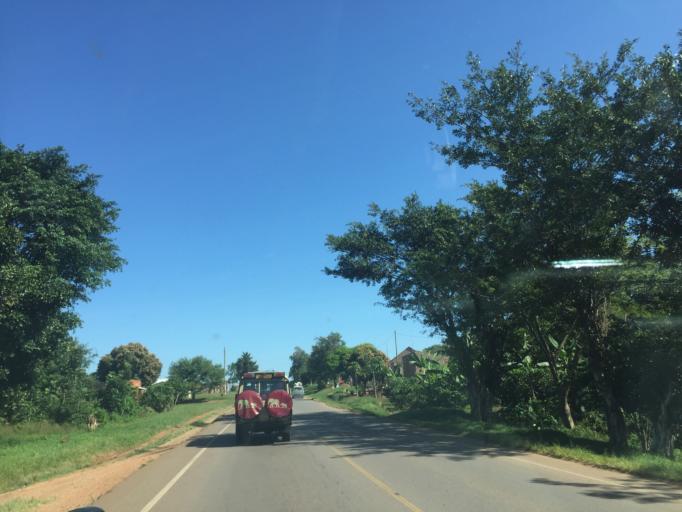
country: UG
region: Central Region
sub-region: Luwero District
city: Wobulenzi
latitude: 0.7610
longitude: 32.5132
